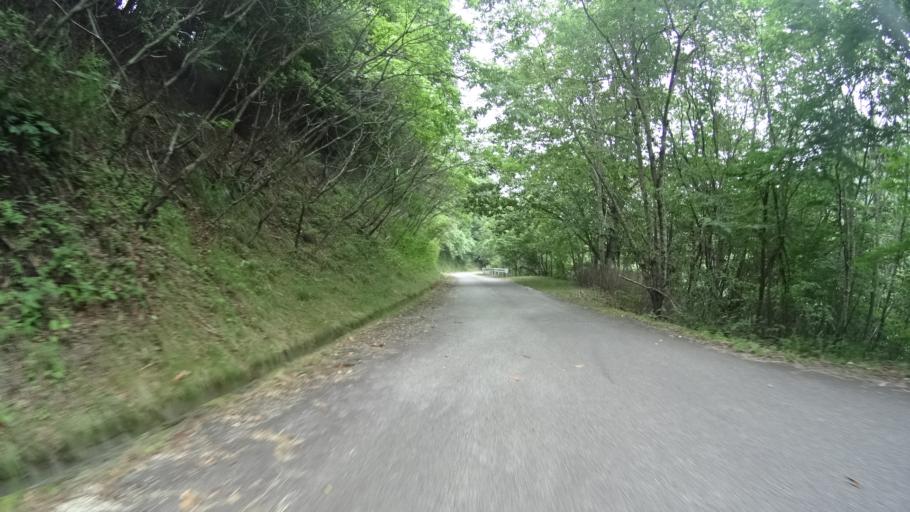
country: JP
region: Yamanashi
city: Kofu-shi
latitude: 35.8259
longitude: 138.5896
